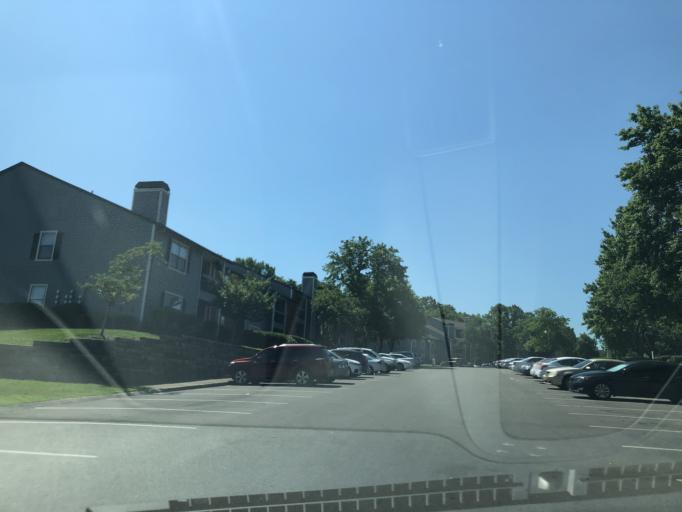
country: US
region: Tennessee
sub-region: Williamson County
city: Nolensville
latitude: 36.0415
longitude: -86.6676
